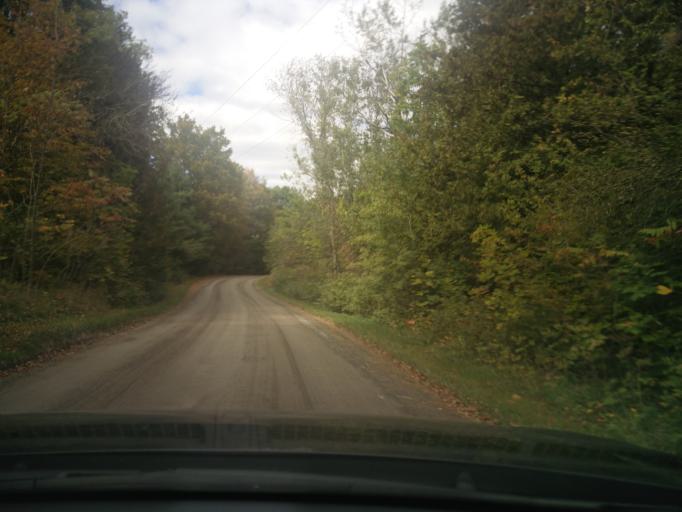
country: CA
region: Ontario
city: Perth
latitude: 44.6651
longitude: -76.5803
